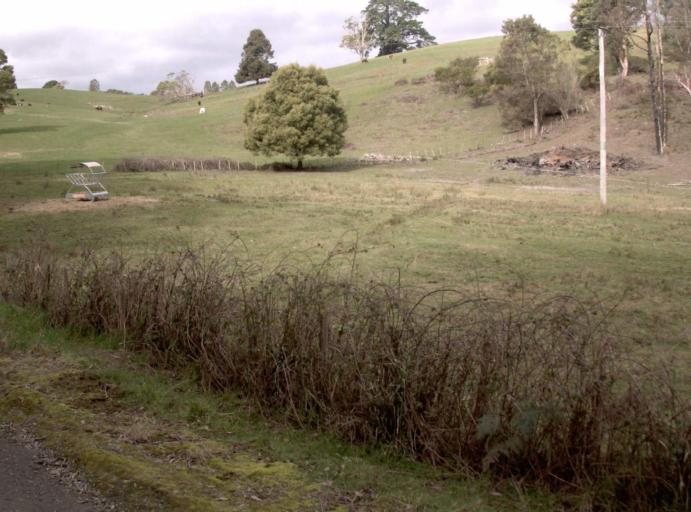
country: AU
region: Tasmania
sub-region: Launceston
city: Mayfield
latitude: -41.2713
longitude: 147.1742
